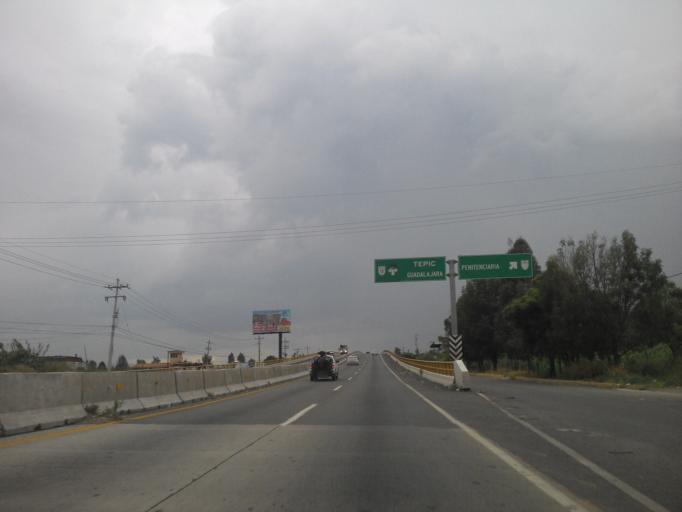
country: MX
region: Jalisco
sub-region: Tonala
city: Paseo Puente Viejo
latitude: 20.5714
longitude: -103.1948
